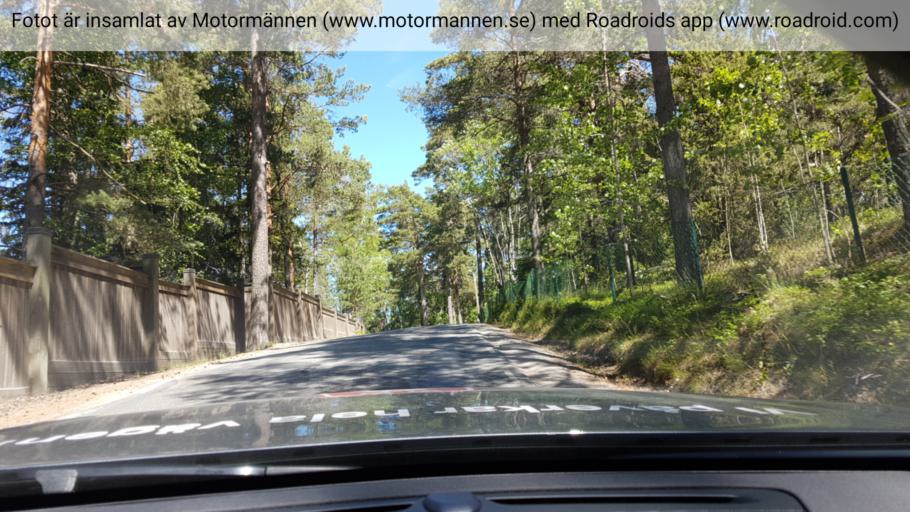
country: SE
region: Stockholm
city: Dalaro
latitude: 59.1495
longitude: 18.4329
